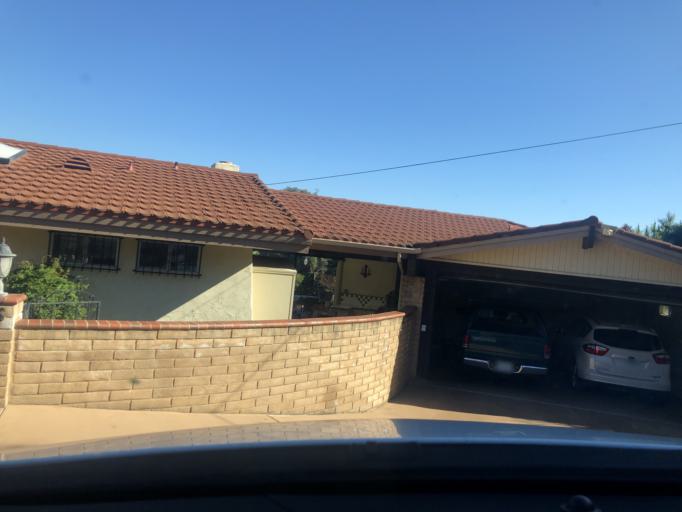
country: US
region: California
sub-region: San Diego County
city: Casa de Oro-Mount Helix
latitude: 32.7739
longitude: -116.9454
